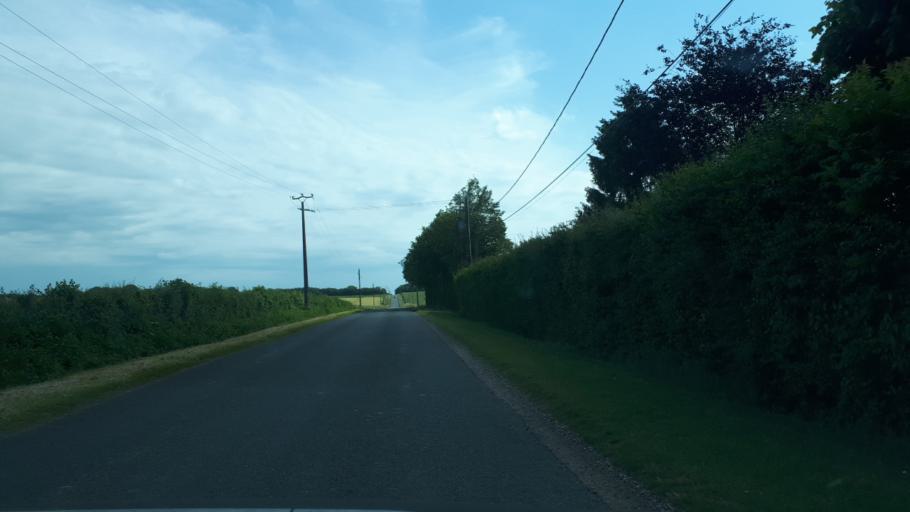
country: FR
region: Centre
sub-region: Departement du Cher
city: Henrichemont
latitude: 47.3715
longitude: 2.5935
